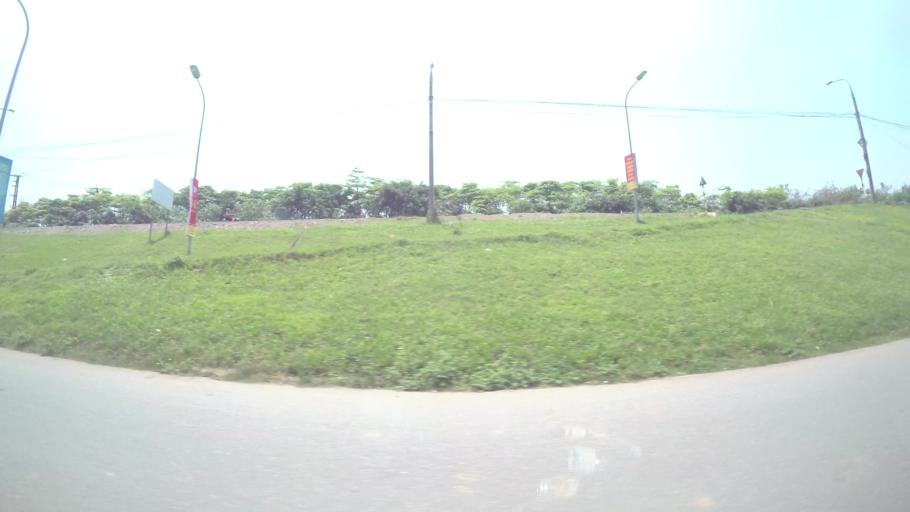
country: VN
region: Ha Noi
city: Hoan Kiem
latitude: 21.0232
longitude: 105.8878
